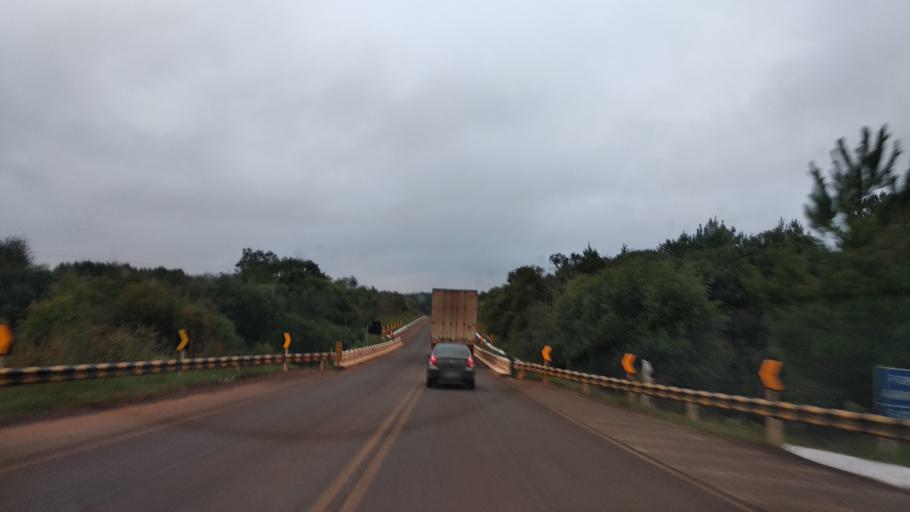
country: BR
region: Santa Catarina
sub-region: Campos Novos
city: Campos Novos
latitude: -27.3948
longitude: -51.0487
